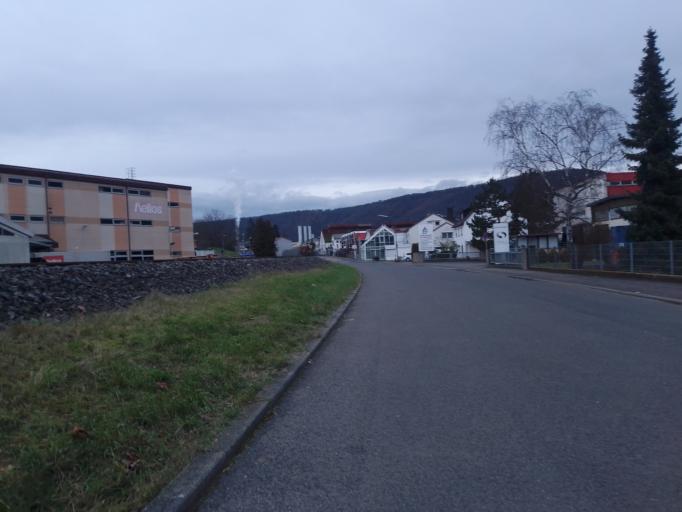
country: DE
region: Bavaria
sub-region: Regierungsbezirk Unterfranken
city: Hasloch
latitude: 49.7860
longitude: 9.5029
